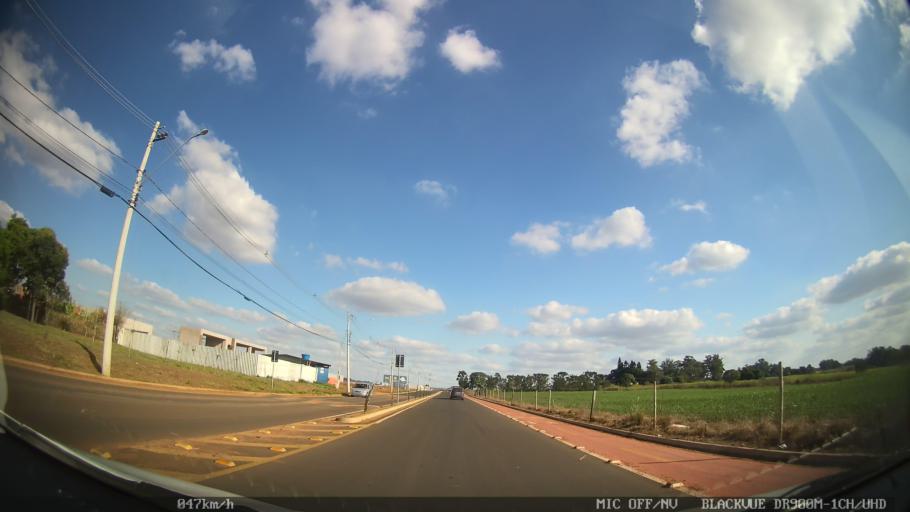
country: BR
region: Sao Paulo
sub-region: Nova Odessa
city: Nova Odessa
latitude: -22.8094
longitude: -47.3204
